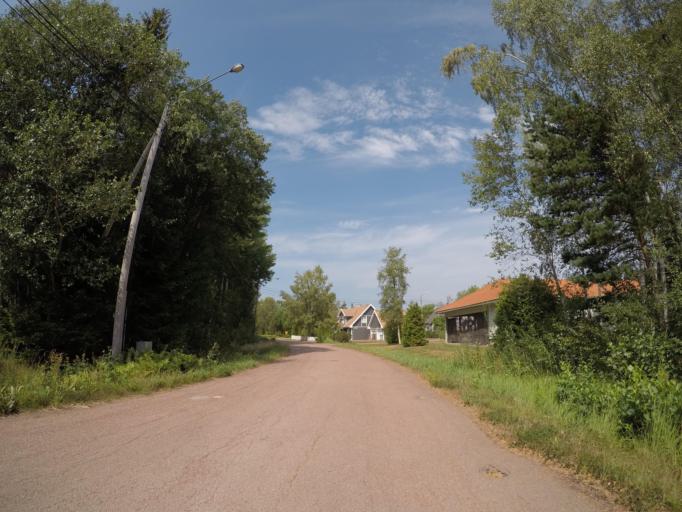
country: AX
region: Alands landsbygd
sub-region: Finstroem
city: Finstroem
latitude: 60.2354
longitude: 19.9735
